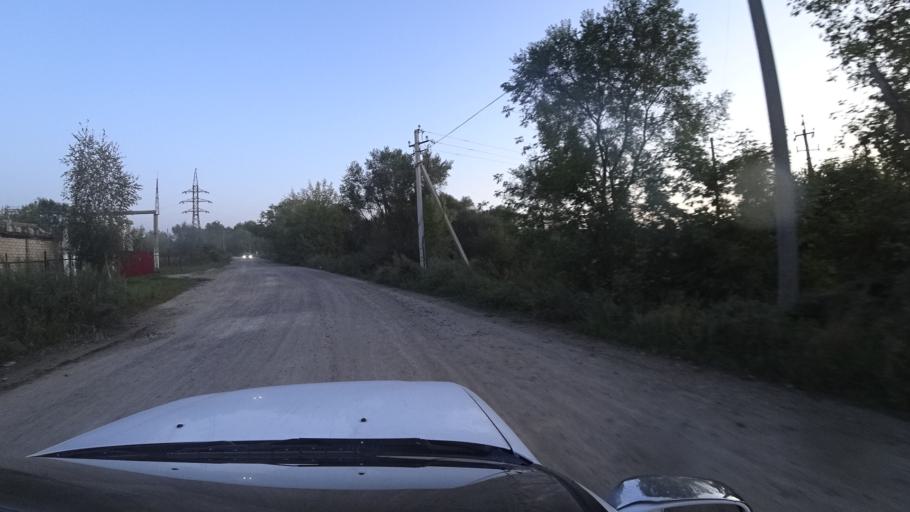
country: RU
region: Primorskiy
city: Dal'nerechensk
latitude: 45.9343
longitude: 133.7580
